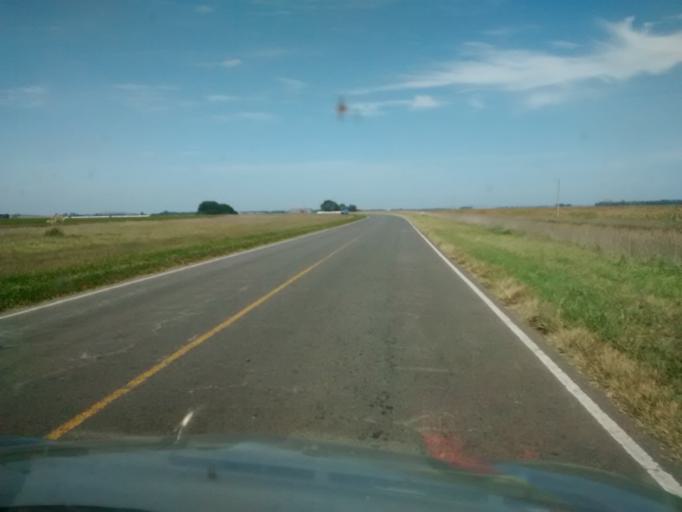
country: AR
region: Buenos Aires
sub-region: Partido de Balcarce
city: Balcarce
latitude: -37.6165
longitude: -58.5007
